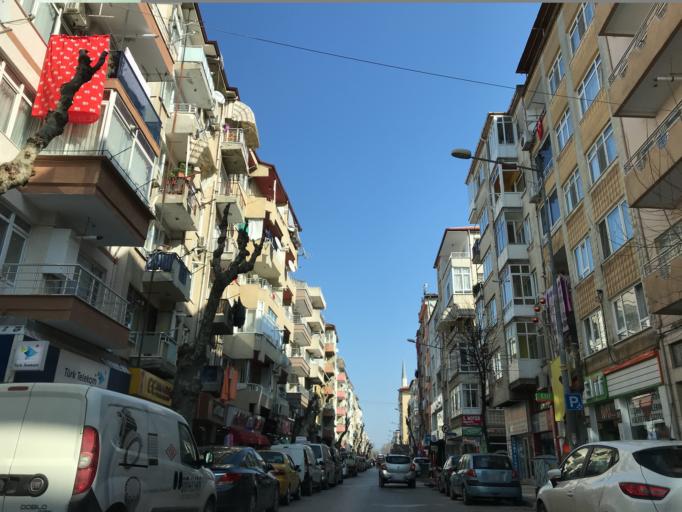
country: TR
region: Yalova
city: Yalova
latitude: 40.6560
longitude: 29.2756
